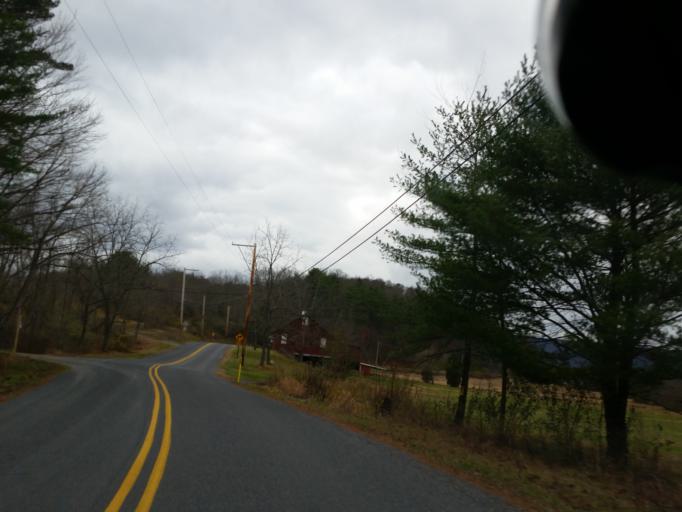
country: US
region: Pennsylvania
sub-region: Union County
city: New Columbia
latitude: 41.0290
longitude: -76.9378
